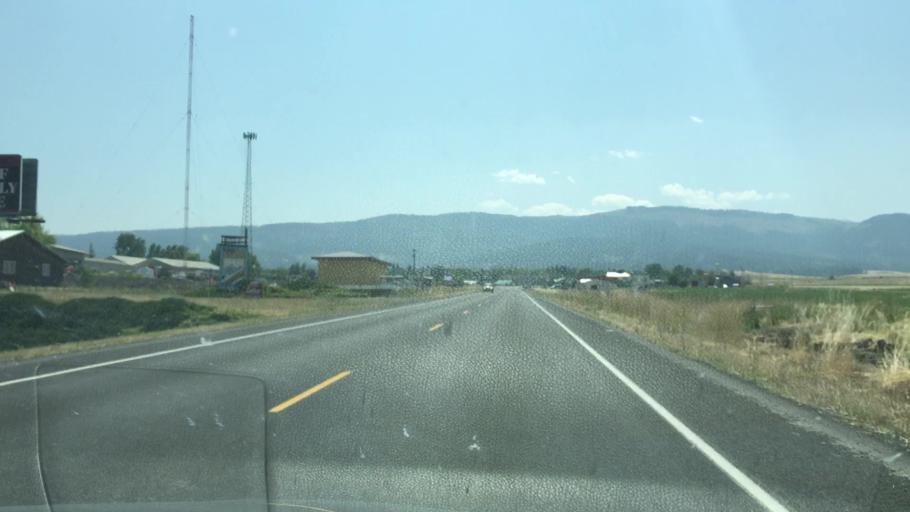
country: US
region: Idaho
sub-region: Idaho County
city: Grangeville
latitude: 45.9322
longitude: -116.1325
